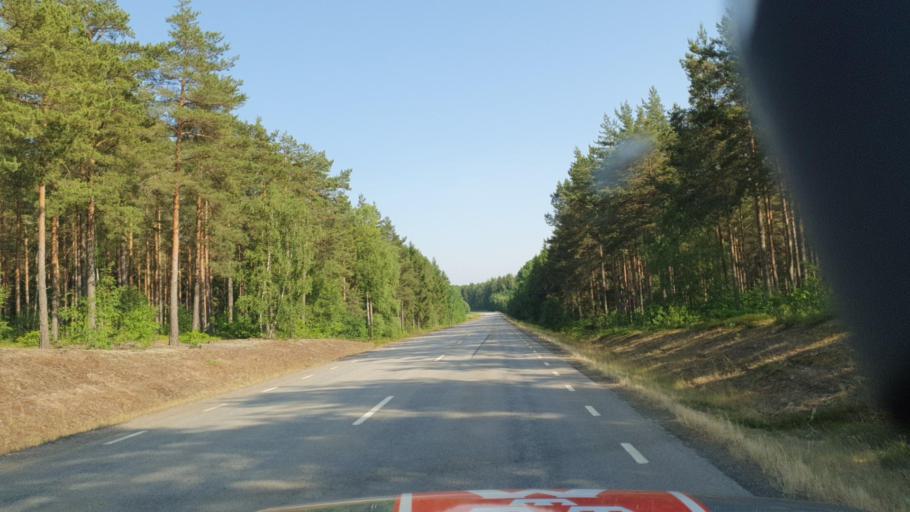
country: SE
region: Kalmar
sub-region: Kalmar Kommun
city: Ljungbyholm
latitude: 56.6452
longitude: 16.1677
